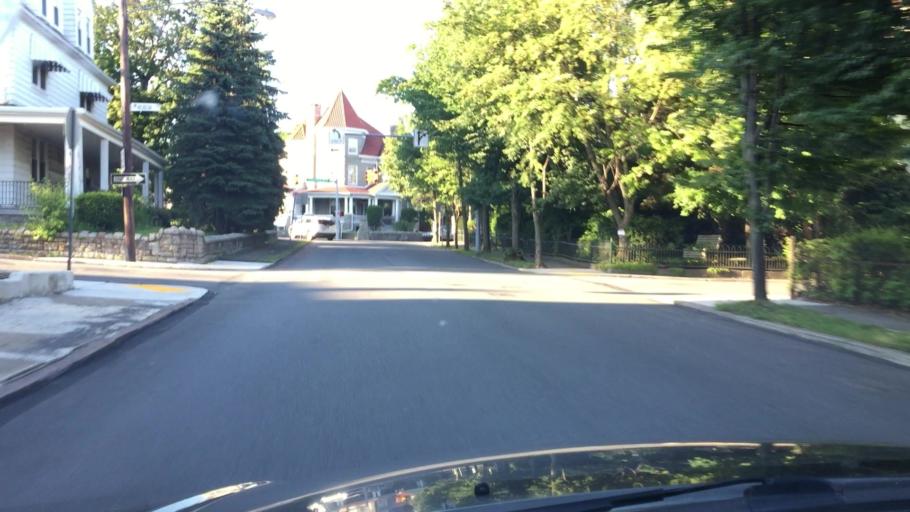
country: US
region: Pennsylvania
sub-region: Luzerne County
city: Hazleton
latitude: 40.9597
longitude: -75.9730
